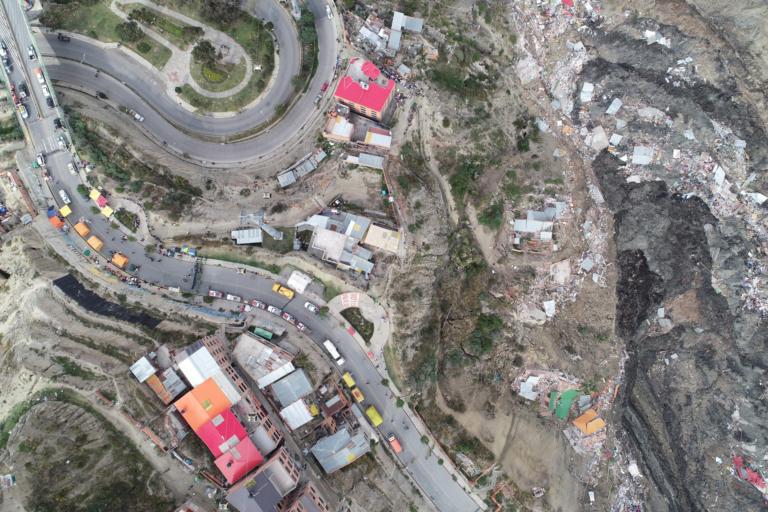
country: BO
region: La Paz
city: La Paz
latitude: -16.5177
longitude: -68.1217
